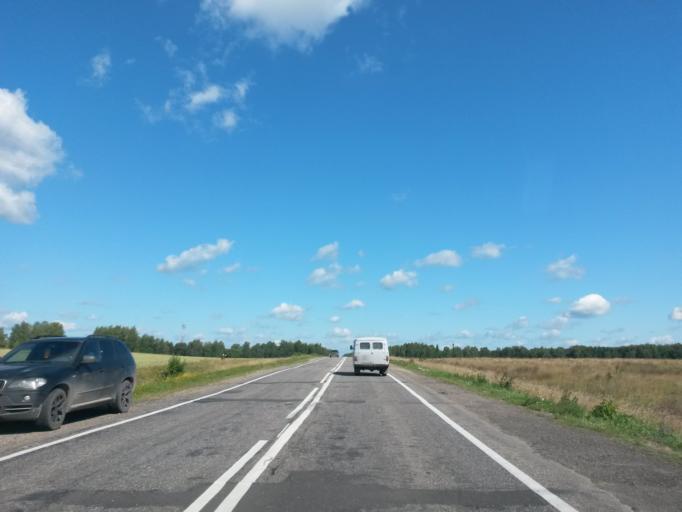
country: RU
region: Jaroslavl
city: Gavrilov-Yam
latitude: 57.4019
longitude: 39.9214
